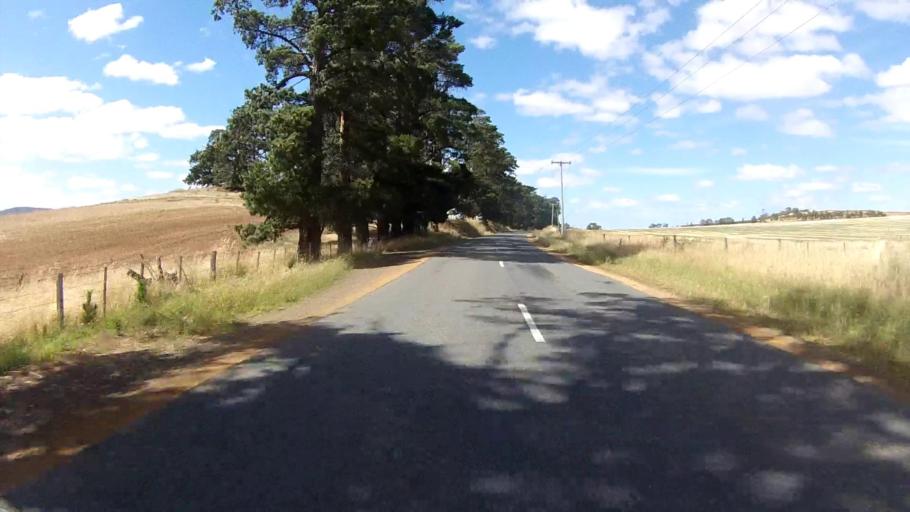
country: AU
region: Tasmania
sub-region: Sorell
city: Sorell
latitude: -42.6371
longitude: 147.4321
